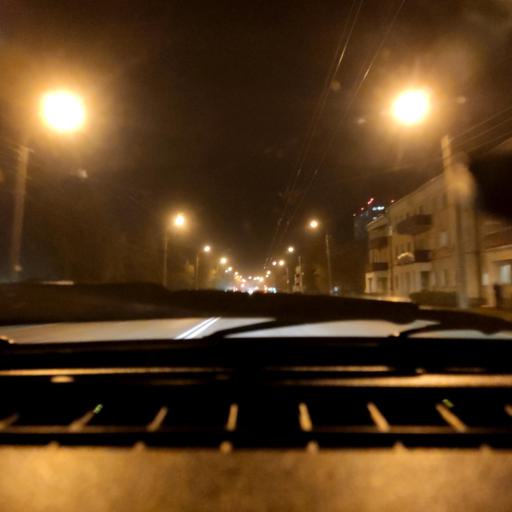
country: RU
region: Bashkortostan
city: Ufa
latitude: 54.7938
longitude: 56.1393
